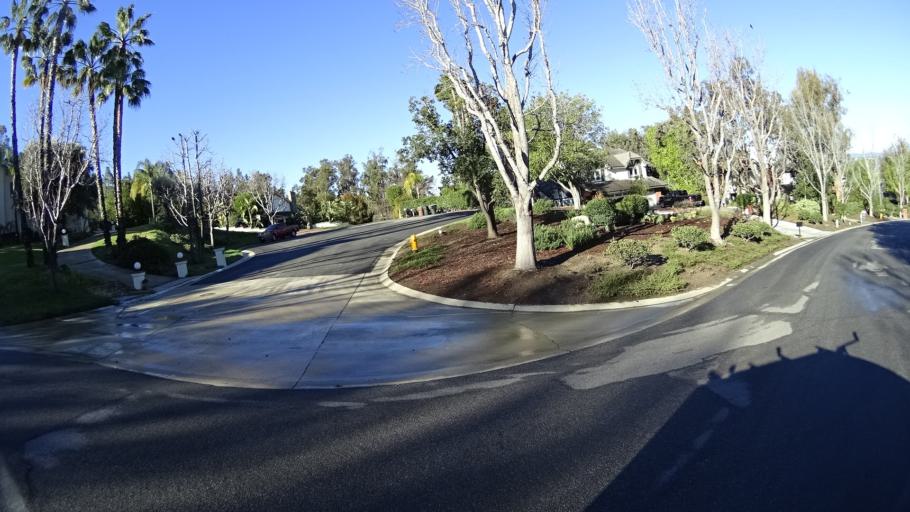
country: US
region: California
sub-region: Orange County
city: Villa Park
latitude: 33.8504
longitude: -117.7656
